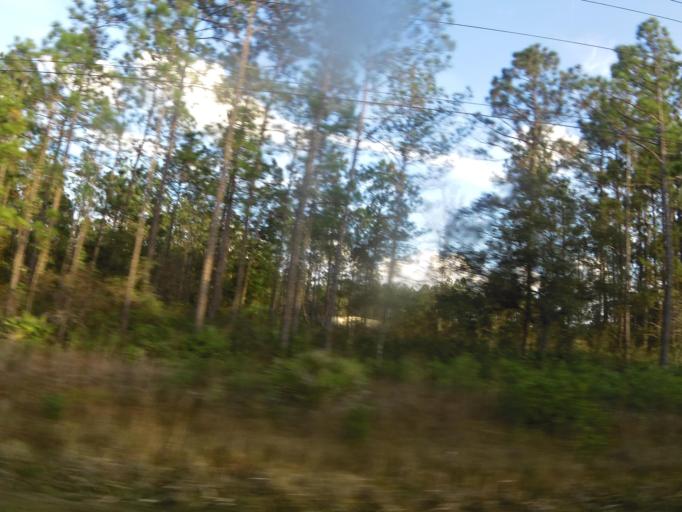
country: US
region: Florida
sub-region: Duval County
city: Baldwin
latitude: 30.1588
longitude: -82.0001
